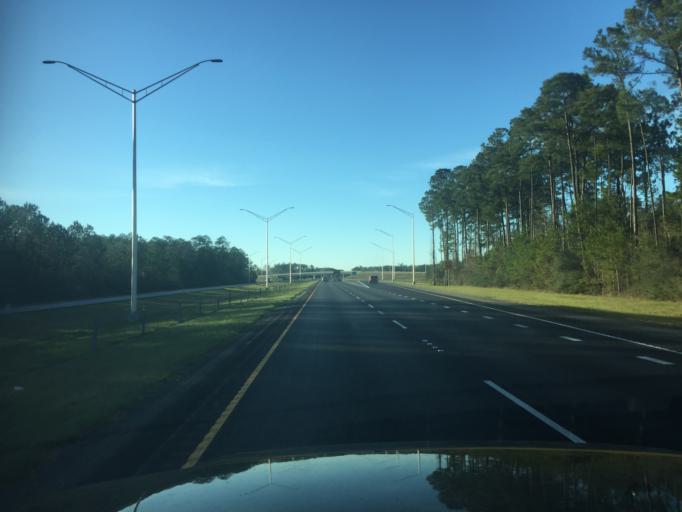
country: US
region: Louisiana
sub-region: Saint Tammany Parish
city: Mandeville
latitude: 30.3901
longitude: -89.9970
